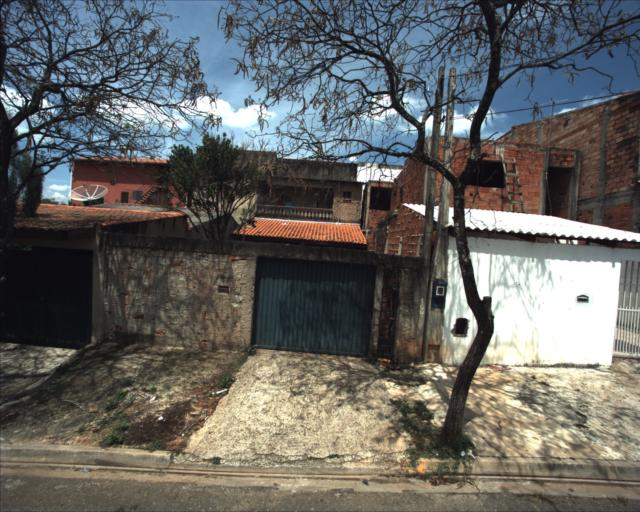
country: BR
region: Sao Paulo
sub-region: Sorocaba
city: Sorocaba
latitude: -23.4107
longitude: -47.4092
